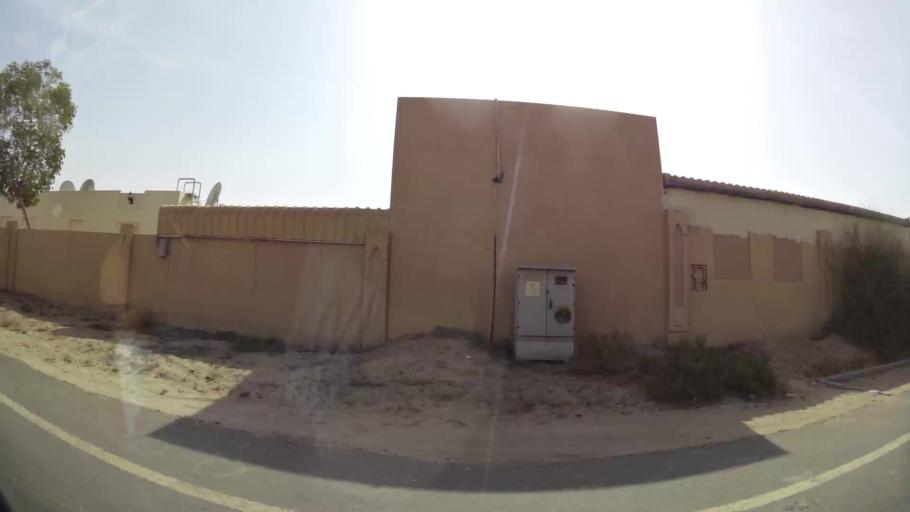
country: AE
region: Ash Shariqah
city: Sharjah
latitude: 25.2570
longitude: 55.4335
